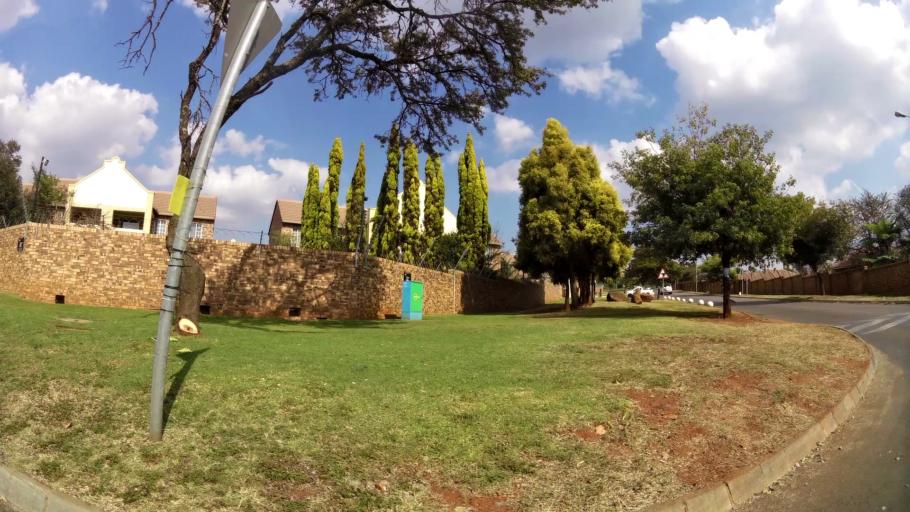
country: ZA
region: Gauteng
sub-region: City of Tshwane Metropolitan Municipality
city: Pretoria
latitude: -25.8012
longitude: 28.3242
